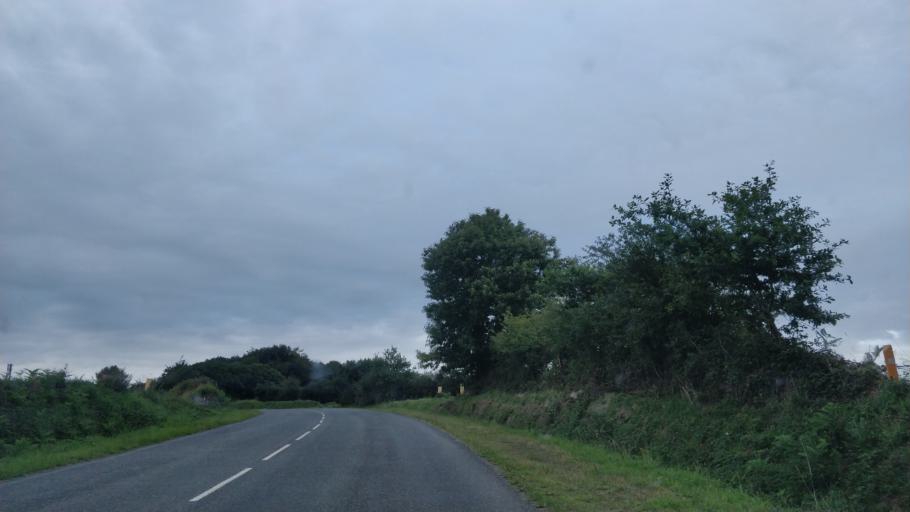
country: FR
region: Brittany
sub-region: Departement du Finistere
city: Loperhet
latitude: 48.3881
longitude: -4.3088
